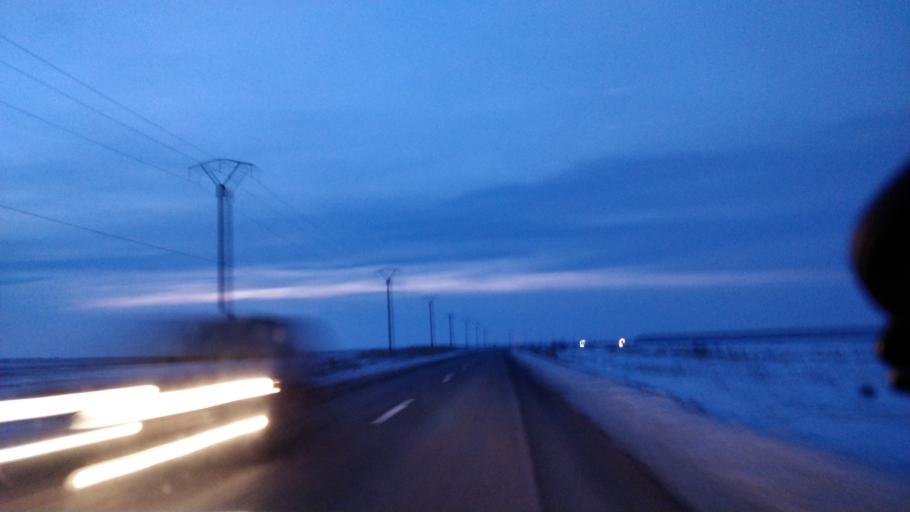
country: RO
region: Vrancea
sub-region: Comuna Vulturu
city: Vadu Rosca
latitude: 45.5942
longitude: 27.4725
